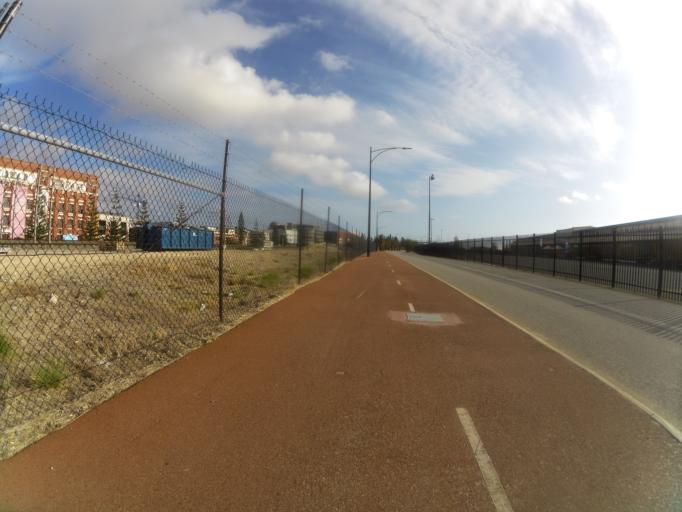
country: AU
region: Western Australia
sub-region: Fremantle
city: North Fremantle
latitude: -32.0465
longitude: 115.7497
